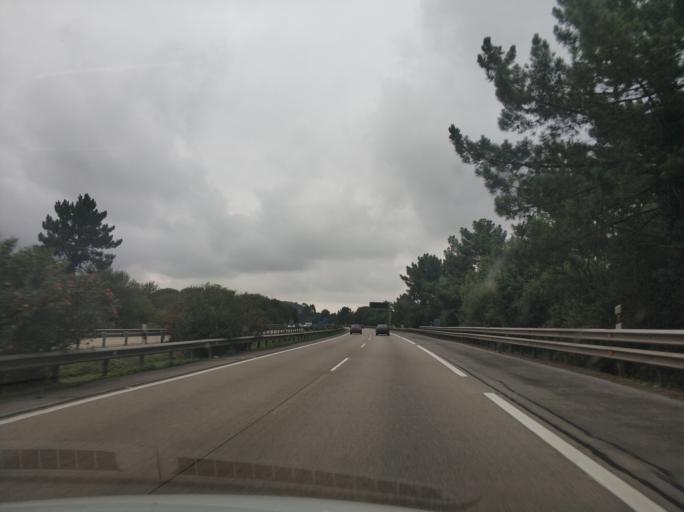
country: ES
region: Asturias
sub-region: Province of Asturias
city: Corvera de Asturias
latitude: 43.5250
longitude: -5.8246
